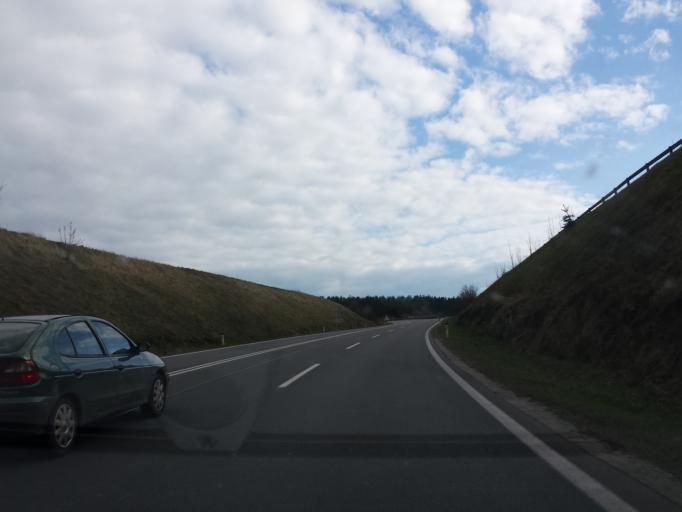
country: AT
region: Lower Austria
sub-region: Politischer Bezirk Krems
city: Rastenfeld
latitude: 48.5436
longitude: 15.3692
